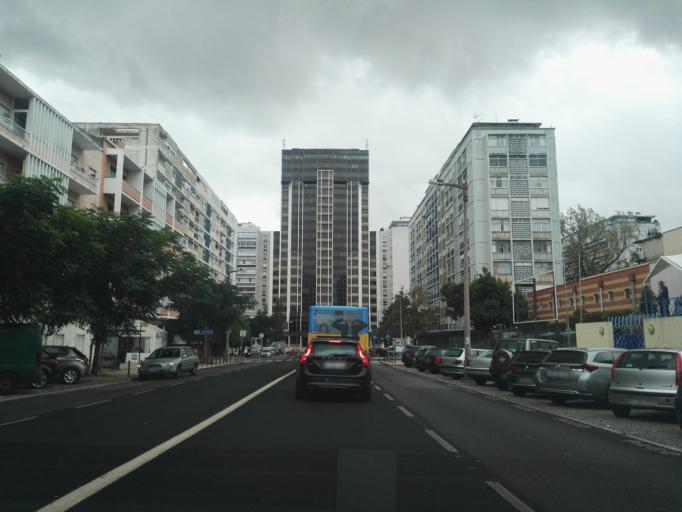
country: PT
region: Lisbon
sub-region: Lisbon
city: Lisbon
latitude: 38.7506
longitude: -9.1374
